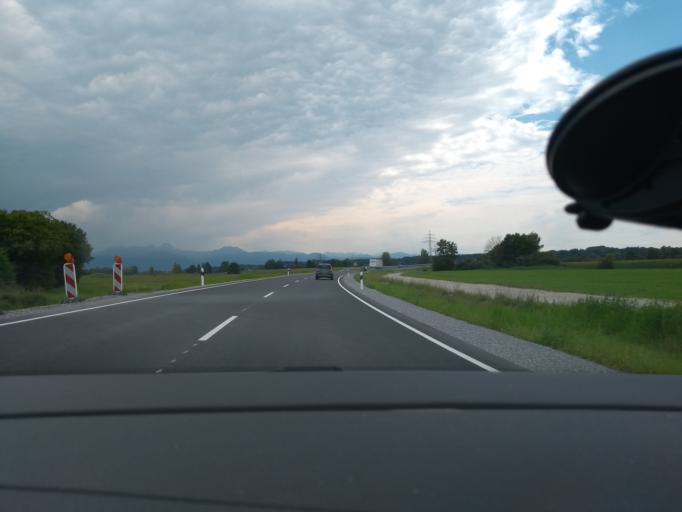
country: DE
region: Bavaria
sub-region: Upper Bavaria
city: Schechen
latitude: 47.8998
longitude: 12.1215
